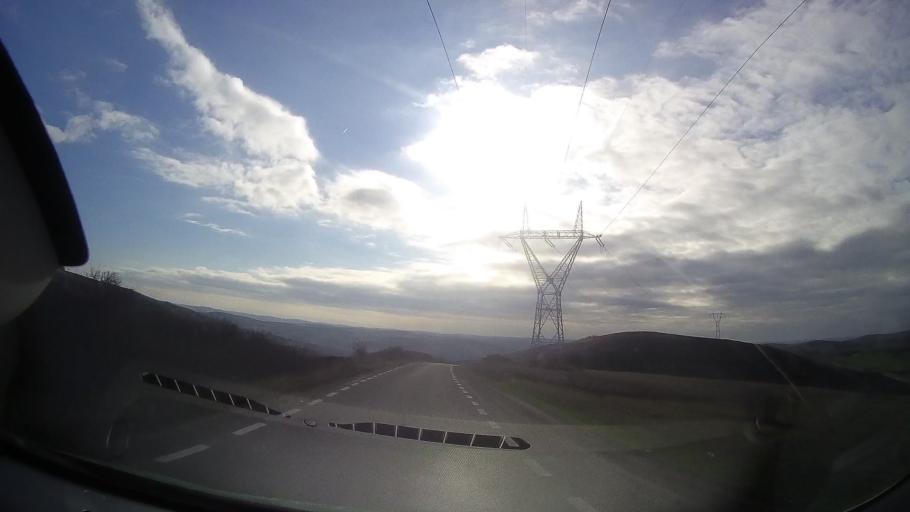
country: RO
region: Mures
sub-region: Comuna Sanger
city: Sanger
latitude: 46.5551
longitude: 24.1608
